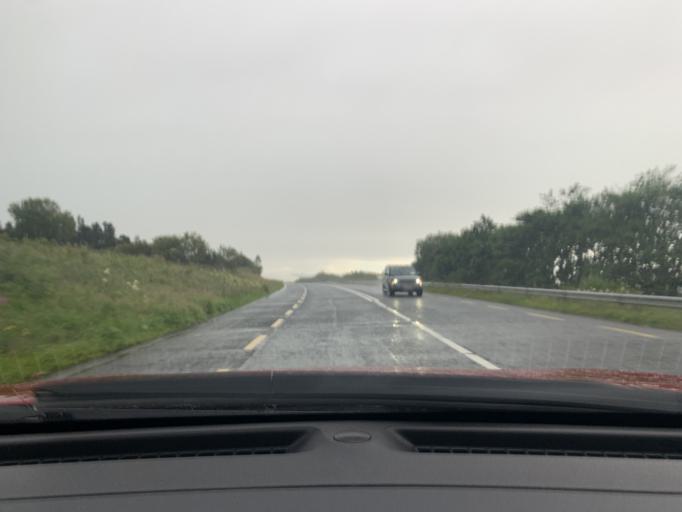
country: IE
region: Ulster
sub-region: County Donegal
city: Letterkenny
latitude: 54.8937
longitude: -7.7312
